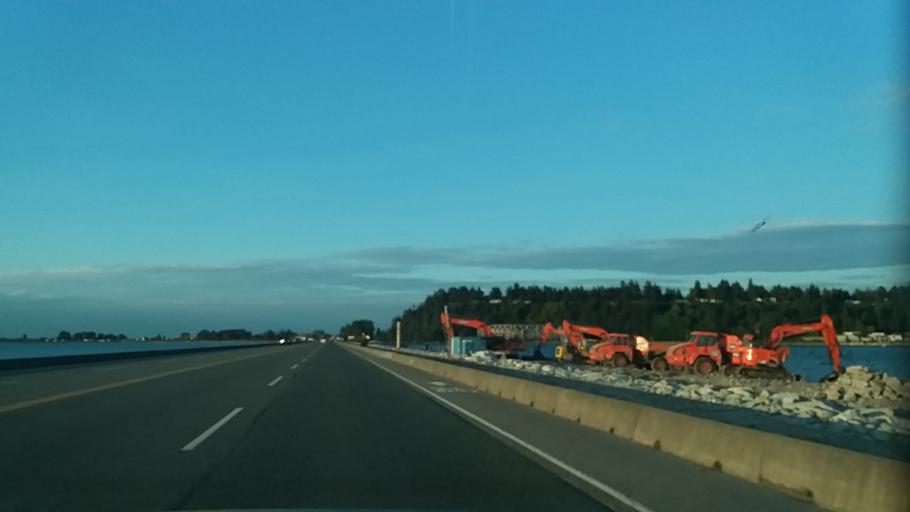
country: US
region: Washington
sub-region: Whatcom County
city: Point Roberts
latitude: 49.0185
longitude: -123.1130
